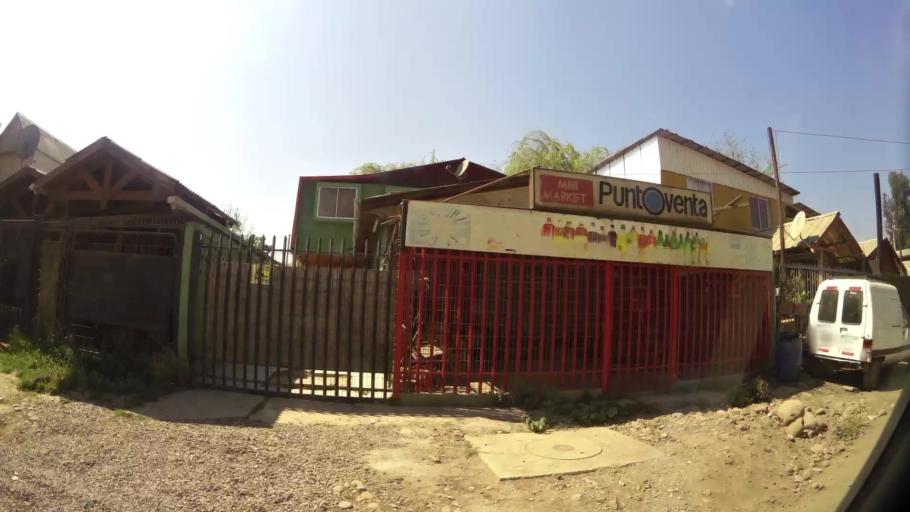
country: CL
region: Santiago Metropolitan
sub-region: Provincia de Talagante
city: Penaflor
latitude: -33.5810
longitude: -70.8123
